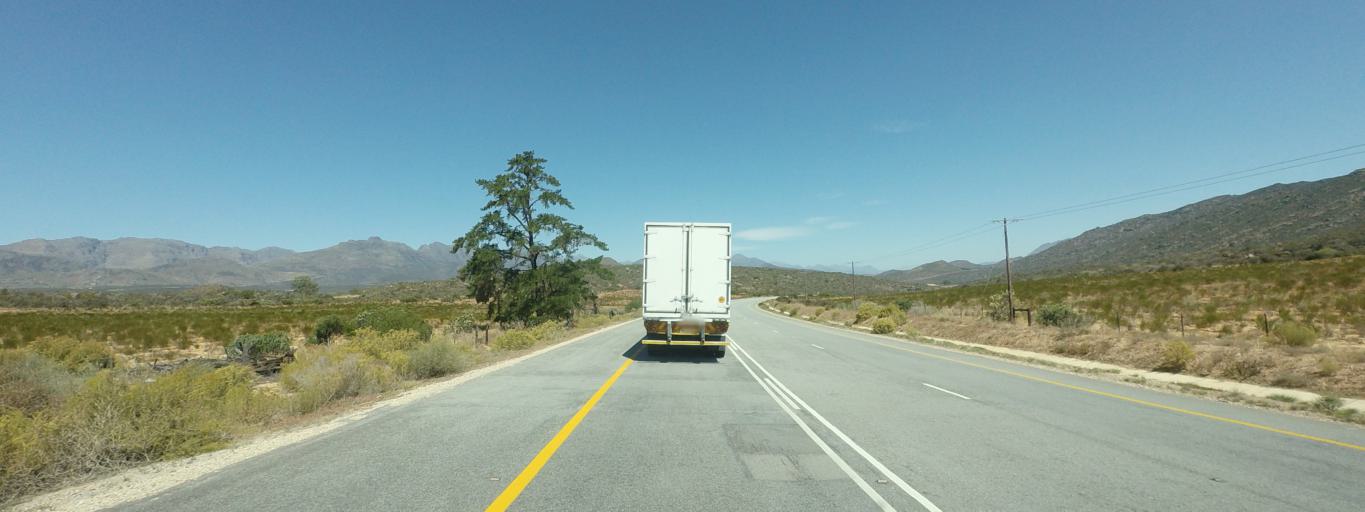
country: ZA
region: Western Cape
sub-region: West Coast District Municipality
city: Clanwilliam
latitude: -32.3271
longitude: 18.9220
